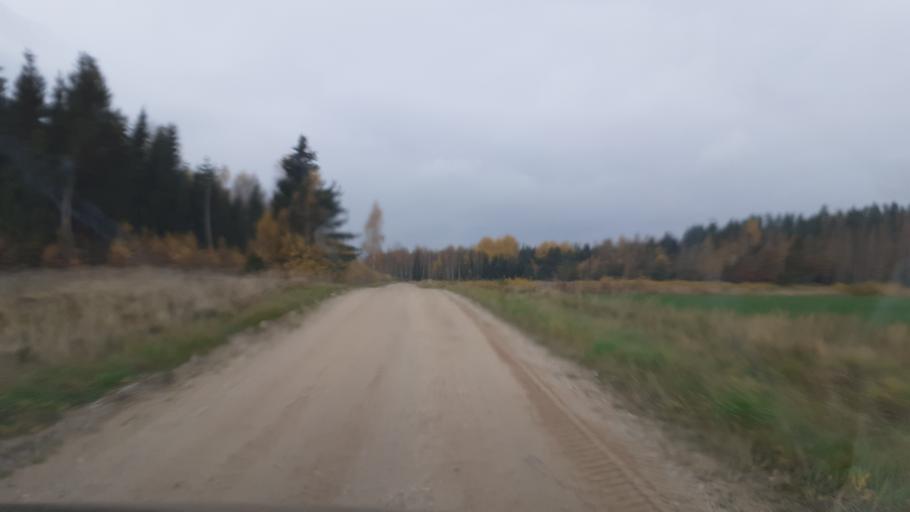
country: LV
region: Saldus Rajons
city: Saldus
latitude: 56.8806
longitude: 22.2853
